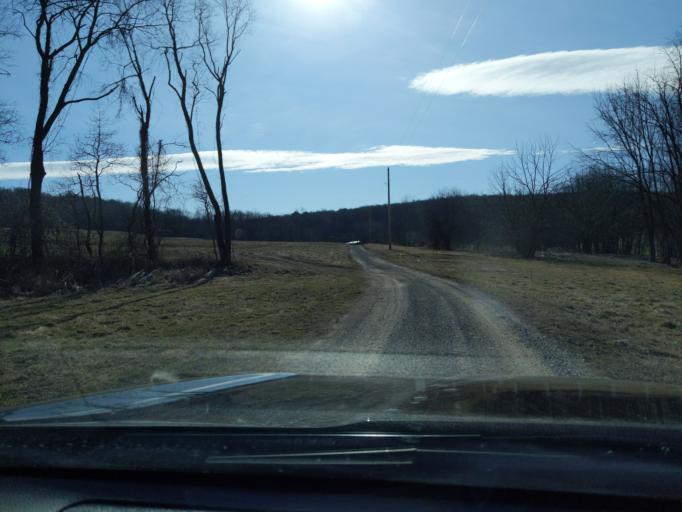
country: US
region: Pennsylvania
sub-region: Blair County
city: Martinsburg
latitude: 40.3912
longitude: -78.2705
